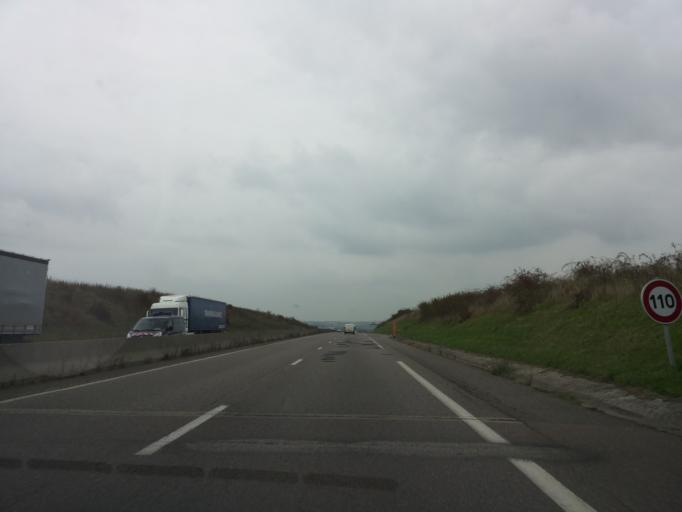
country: FR
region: Lorraine
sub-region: Departement de la Moselle
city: Lorquin
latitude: 48.7025
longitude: 6.9852
